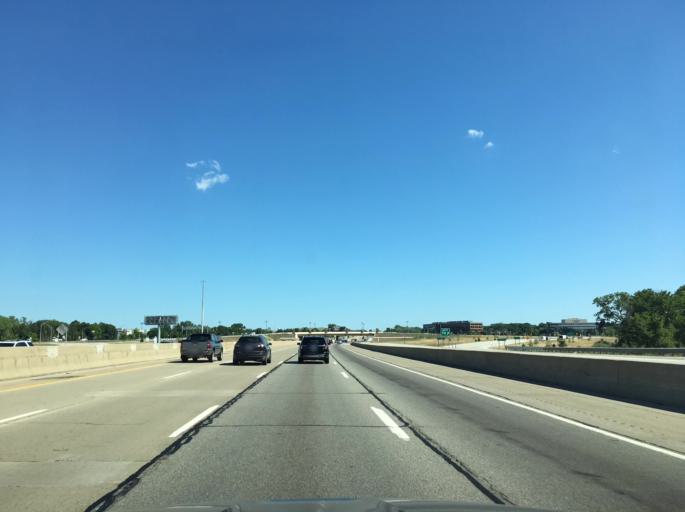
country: US
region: Michigan
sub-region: Oakland County
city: Auburn Hills
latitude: 42.6612
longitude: -83.2406
